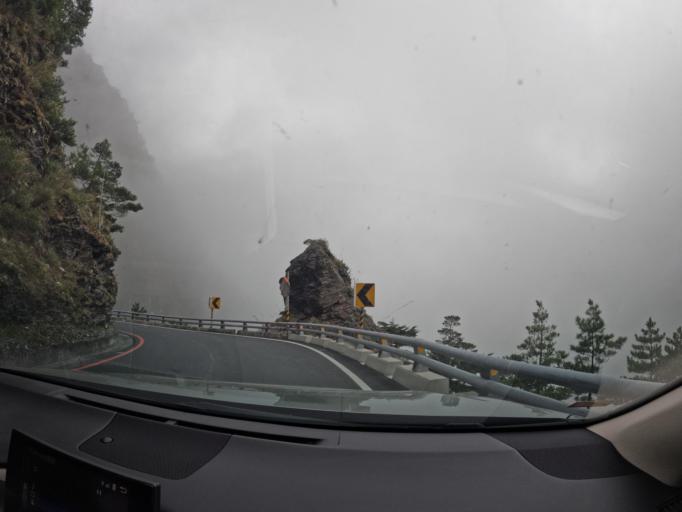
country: TW
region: Taiwan
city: Lugu
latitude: 23.2649
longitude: 120.9771
